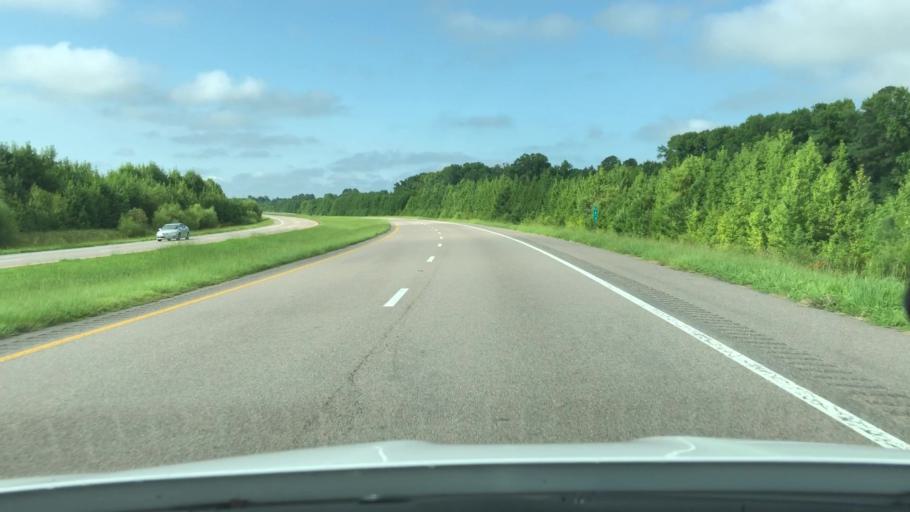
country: US
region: Virginia
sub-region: City of Portsmouth
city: Portsmouth Heights
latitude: 36.6118
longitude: -76.3781
